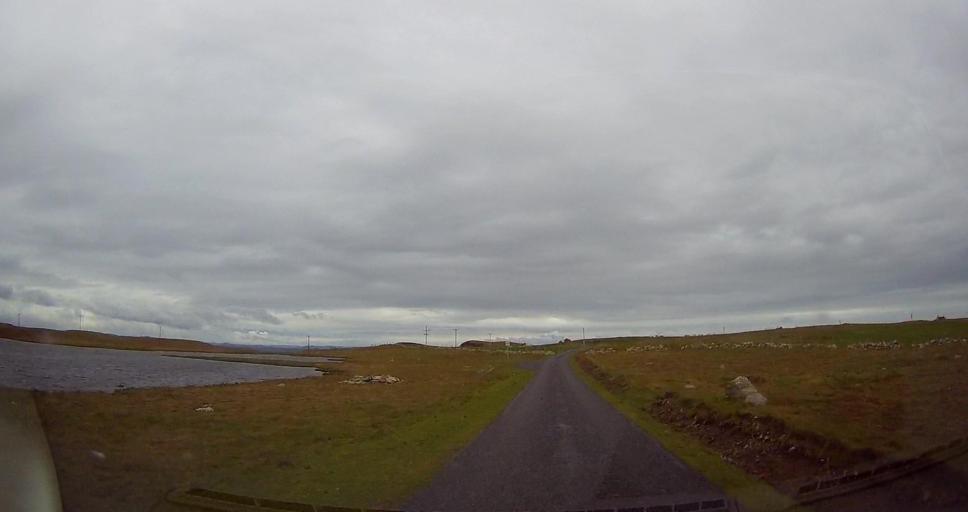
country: GB
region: Scotland
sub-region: Shetland Islands
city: Lerwick
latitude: 60.4850
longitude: -1.6075
